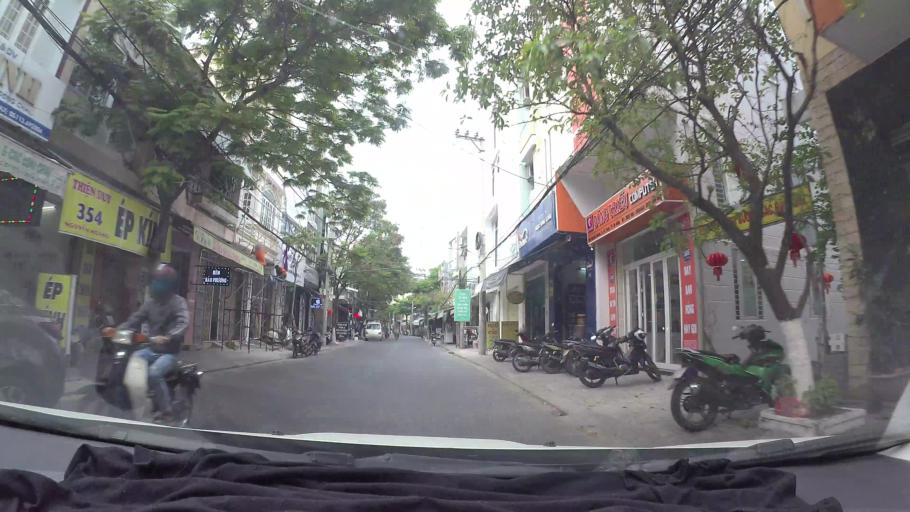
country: VN
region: Da Nang
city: Da Nang
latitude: 16.0560
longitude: 108.2127
